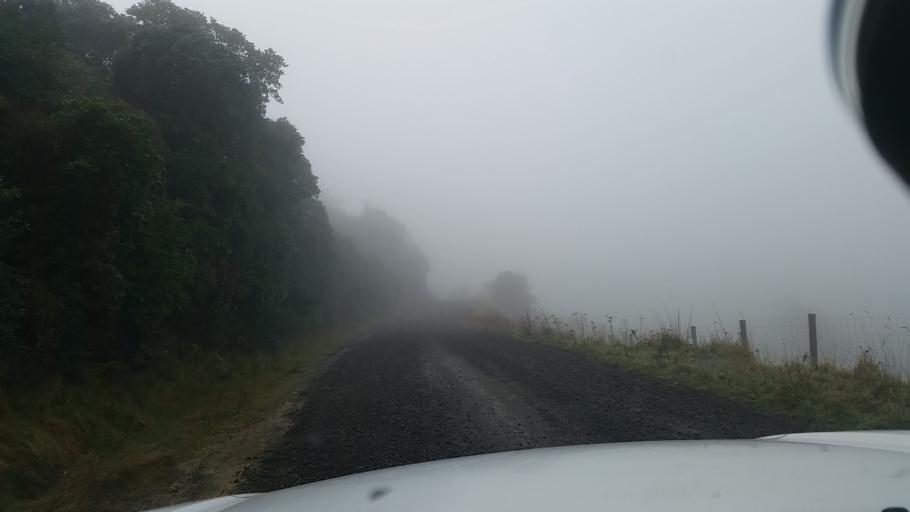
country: NZ
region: Canterbury
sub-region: Christchurch City
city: Christchurch
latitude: -43.7409
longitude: 172.9000
